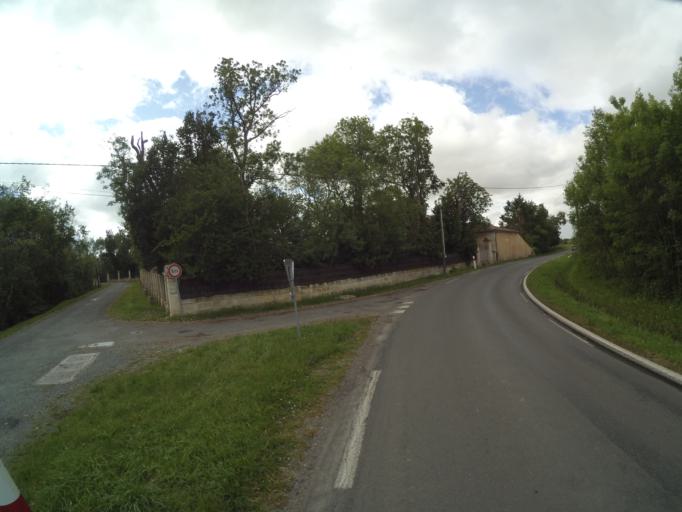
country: FR
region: Aquitaine
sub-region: Departement de la Gironde
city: Ludon-Medoc
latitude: 44.9901
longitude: -0.5854
